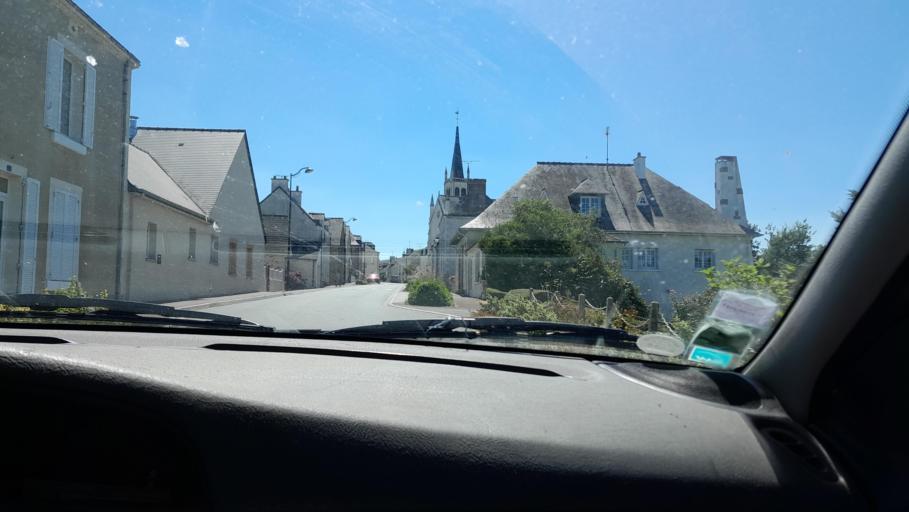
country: FR
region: Pays de la Loire
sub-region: Departement de la Mayenne
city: Congrier
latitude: 47.8432
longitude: -1.1360
